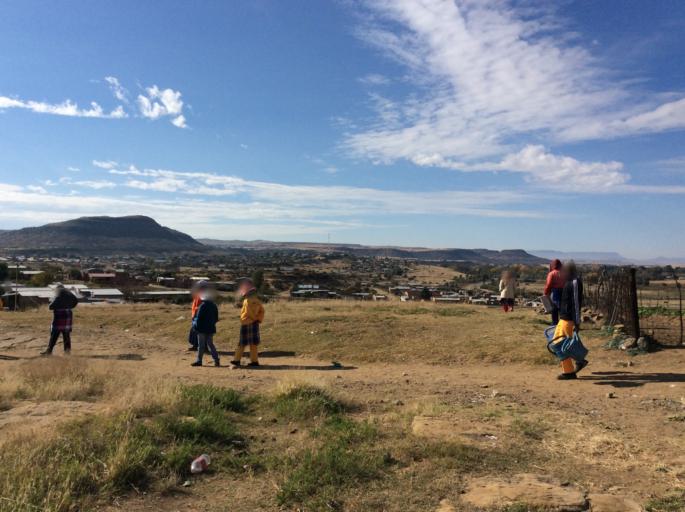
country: LS
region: Mafeteng
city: Mafeteng
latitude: -29.7194
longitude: 27.0142
